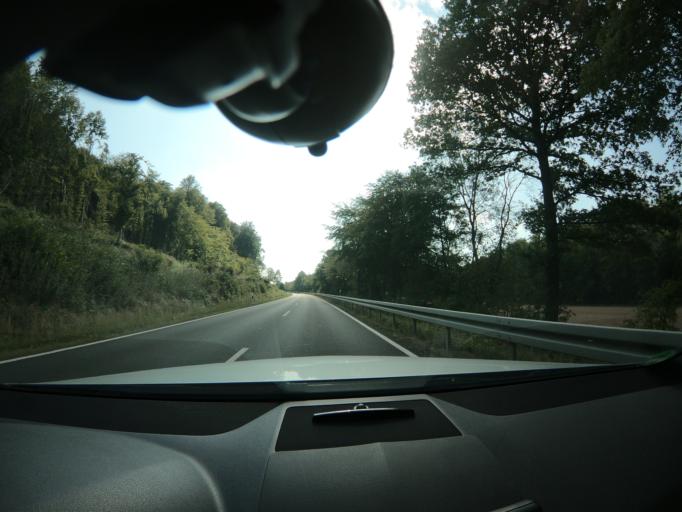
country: DE
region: Hesse
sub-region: Regierungsbezirk Giessen
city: Kirchhain
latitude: 50.8499
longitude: 8.9315
